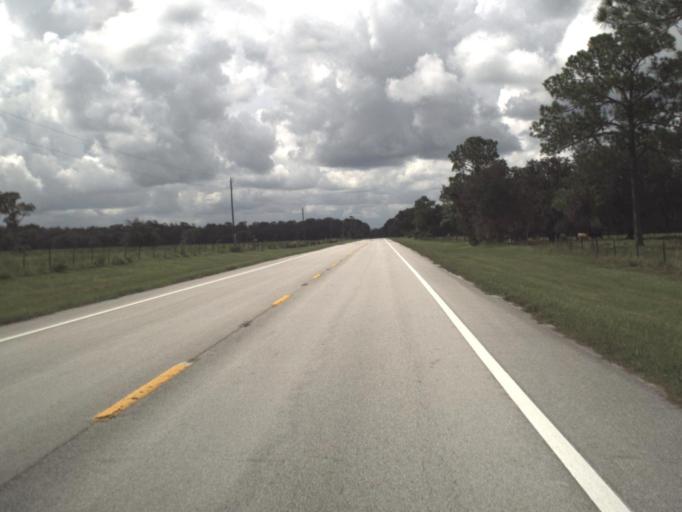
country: US
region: Florida
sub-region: DeSoto County
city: Nocatee
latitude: 27.2022
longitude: -81.9959
